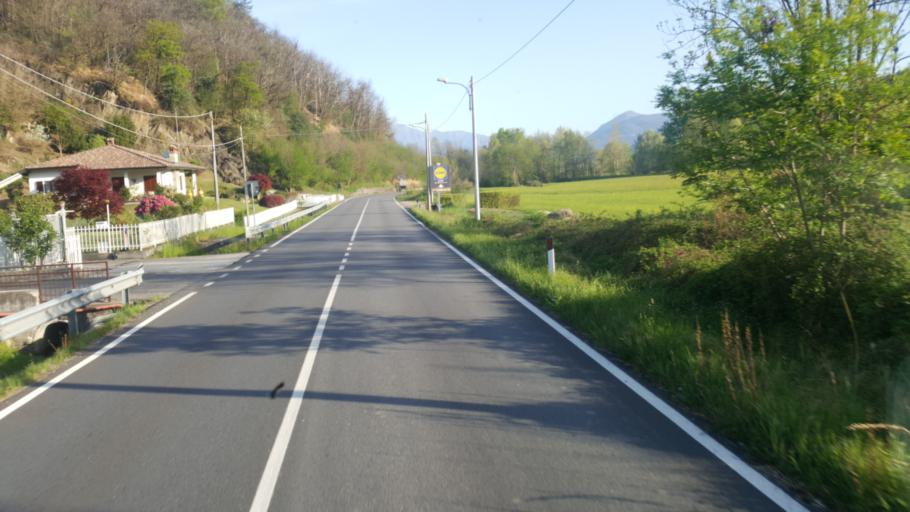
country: IT
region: Lombardy
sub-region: Provincia di Varese
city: Montegrino Valtravaglia
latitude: 45.9698
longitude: 8.7490
